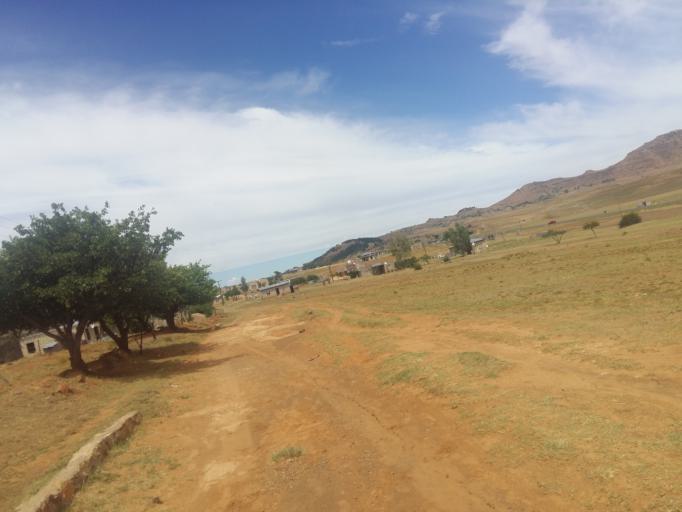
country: LS
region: Mafeteng
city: Mafeteng
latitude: -29.7045
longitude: 27.4312
